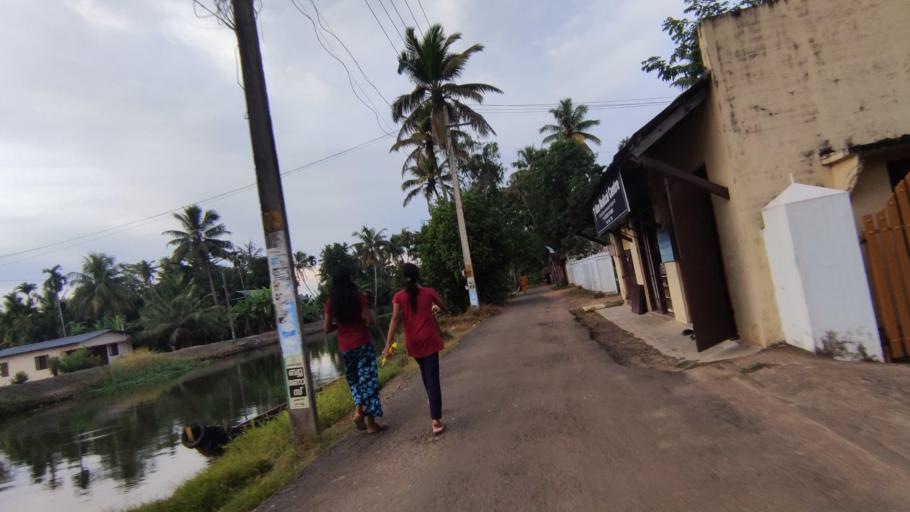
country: IN
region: Kerala
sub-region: Kottayam
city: Kottayam
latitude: 9.6452
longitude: 76.4786
